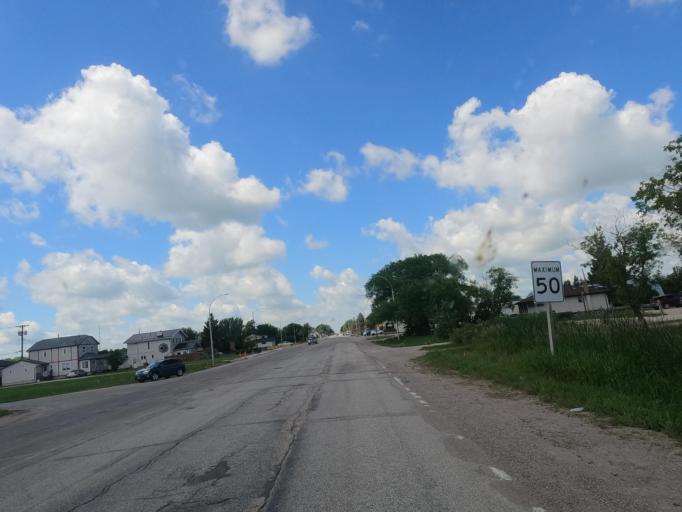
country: CA
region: Manitoba
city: Beausejour
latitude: 50.0618
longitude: -96.5031
